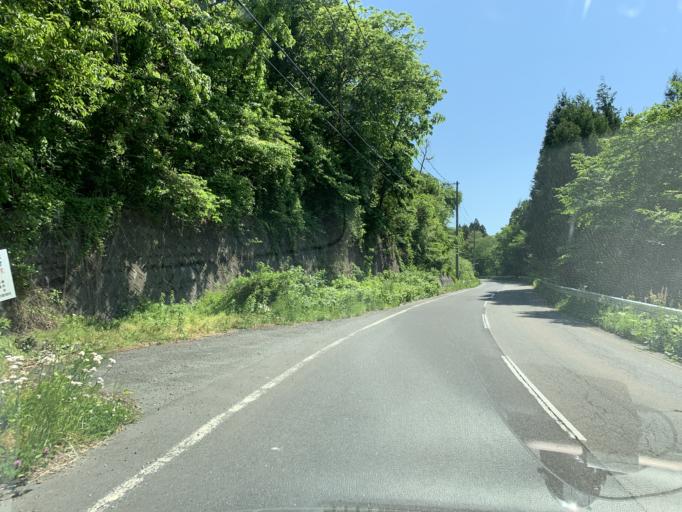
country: JP
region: Iwate
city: Mizusawa
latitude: 39.0645
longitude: 141.0610
